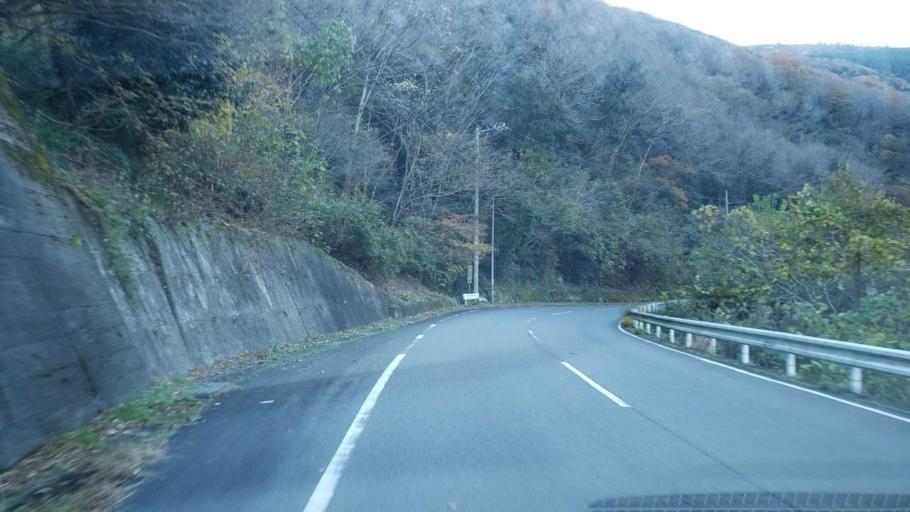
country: JP
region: Tokushima
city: Wakimachi
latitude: 34.0757
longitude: 134.0788
